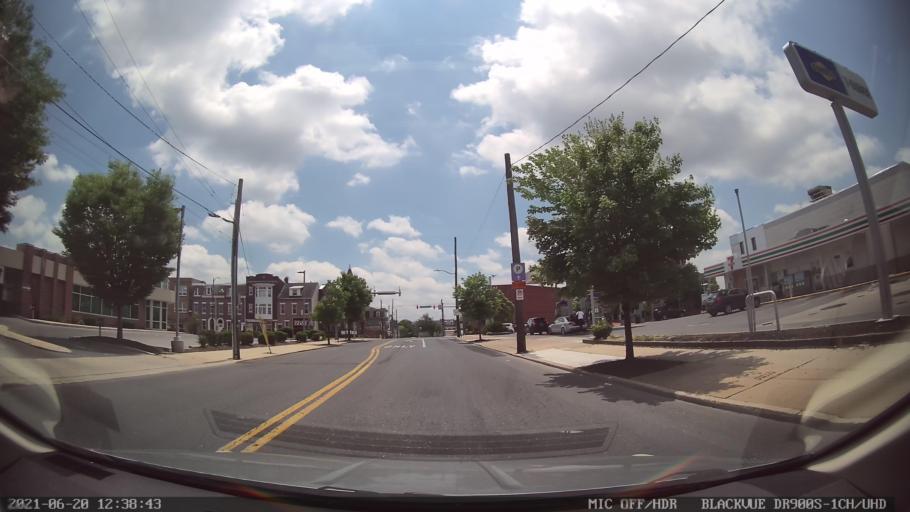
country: US
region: Pennsylvania
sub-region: Lehigh County
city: Allentown
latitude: 40.6000
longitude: -75.4820
